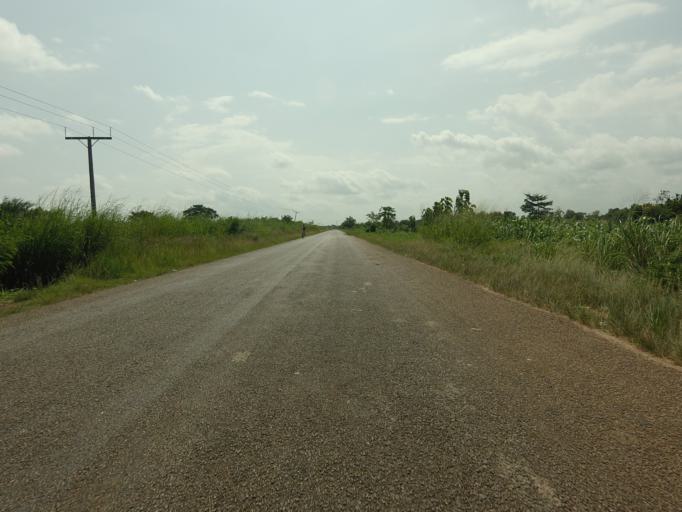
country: TG
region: Maritime
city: Lome
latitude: 6.2436
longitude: 0.9828
